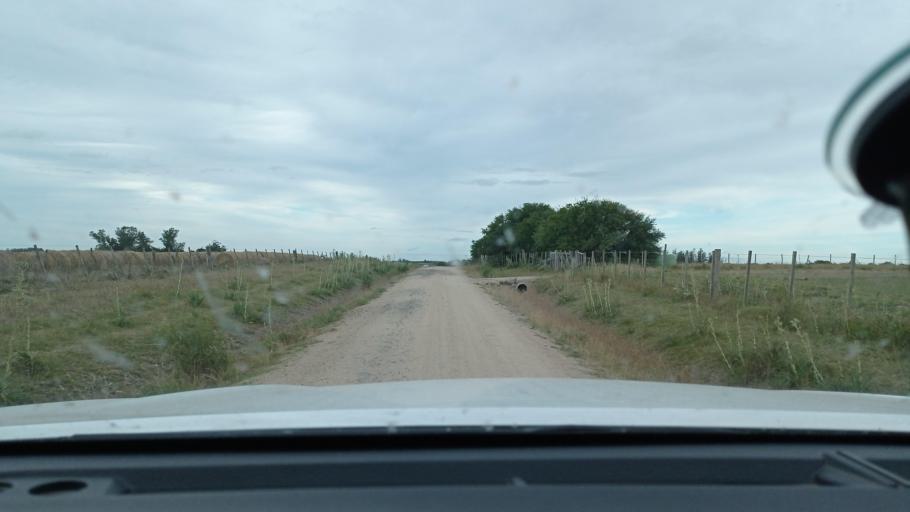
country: UY
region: Florida
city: Casupa
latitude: -34.1481
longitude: -55.7937
